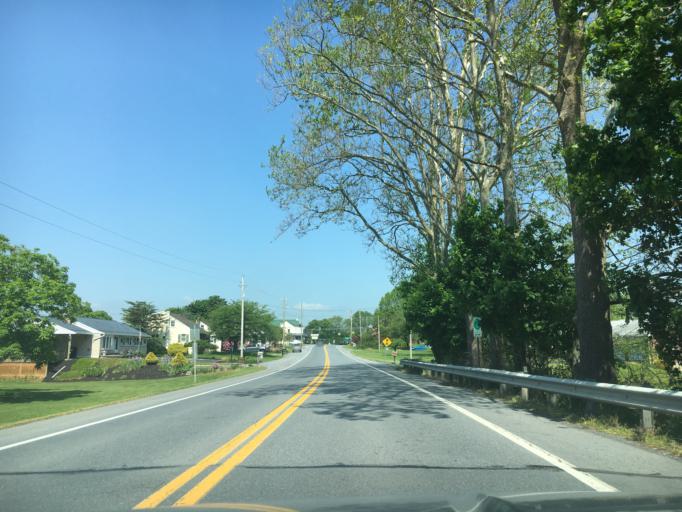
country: US
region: Pennsylvania
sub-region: Berks County
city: Oley
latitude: 40.3828
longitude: -75.7300
